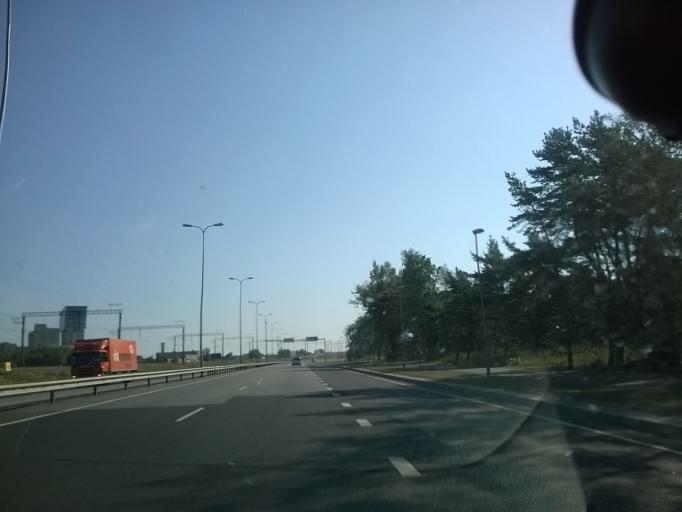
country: EE
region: Harju
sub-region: Tallinna linn
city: Tallinn
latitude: 59.4216
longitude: 24.7750
